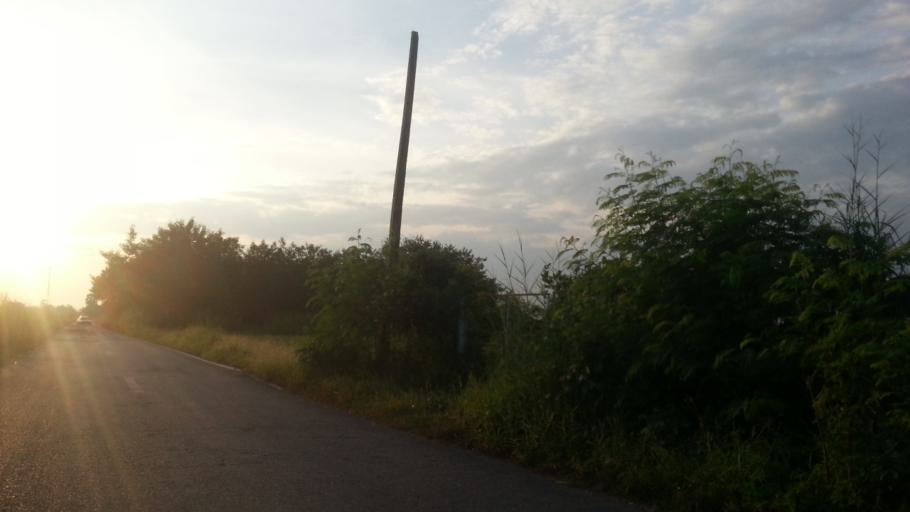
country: TH
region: Pathum Thani
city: Nong Suea
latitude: 14.0412
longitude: 100.8554
